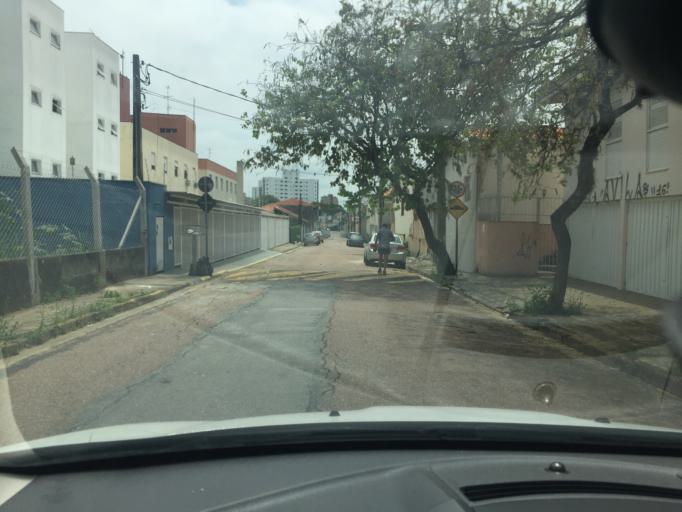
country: BR
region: Sao Paulo
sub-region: Jundiai
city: Jundiai
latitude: -23.1967
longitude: -46.8888
